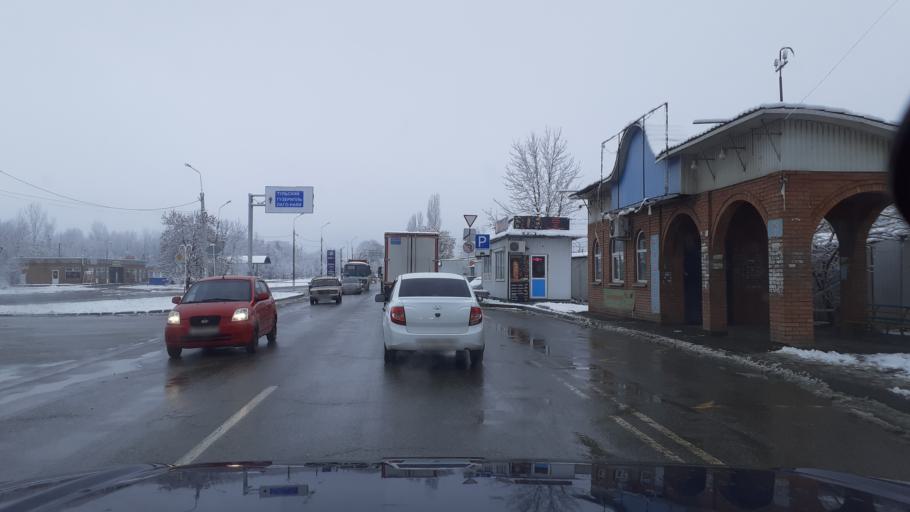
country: RU
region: Adygeya
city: Maykop
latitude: 44.5748
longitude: 40.1334
